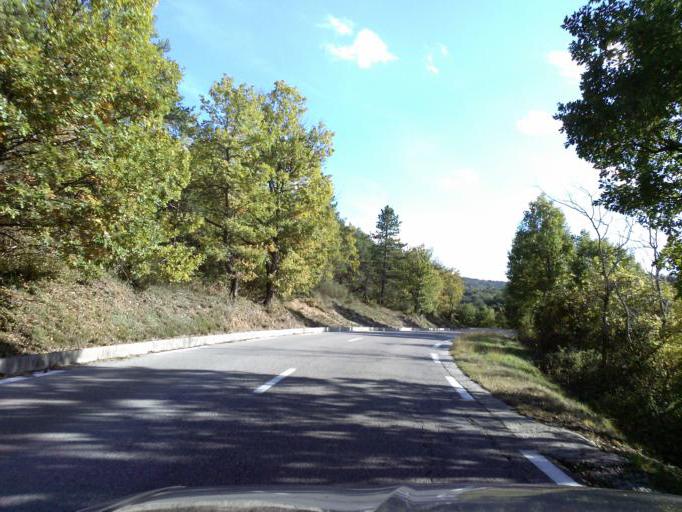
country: FR
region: Provence-Alpes-Cote d'Azur
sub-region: Departement des Alpes-de-Haute-Provence
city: Riez
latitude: 43.9163
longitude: 6.1344
